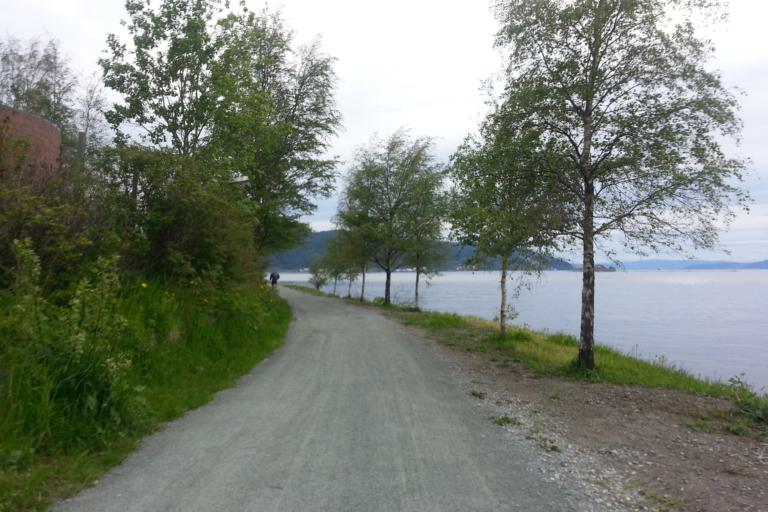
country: NO
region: Sor-Trondelag
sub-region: Trondheim
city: Trondheim
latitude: 63.4484
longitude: 10.4256
